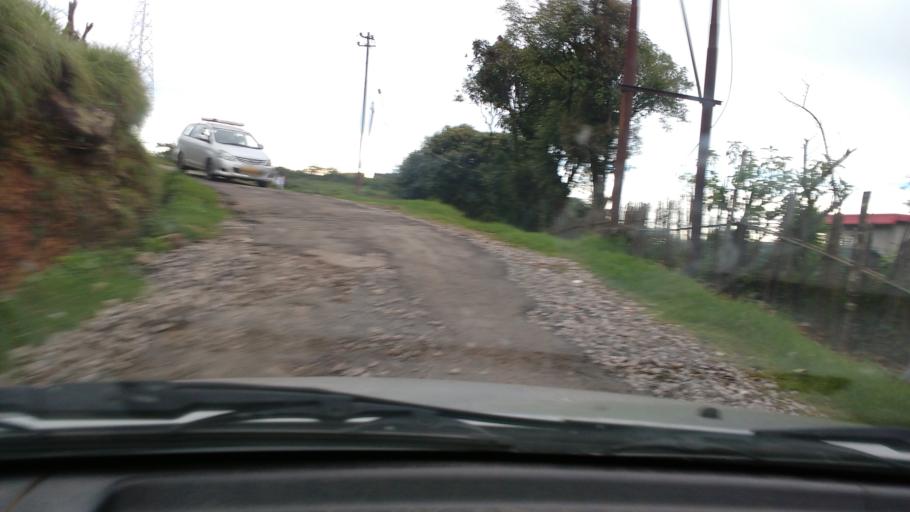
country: IN
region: Meghalaya
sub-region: East Khasi Hills
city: Cherrapunji
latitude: 25.2846
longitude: 91.7156
